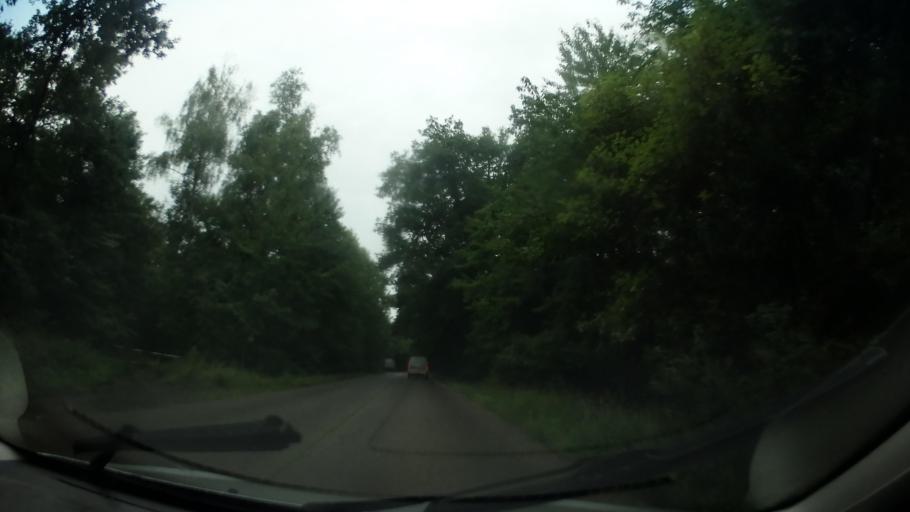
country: CZ
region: Central Bohemia
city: Milovice
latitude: 50.2472
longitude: 14.9287
